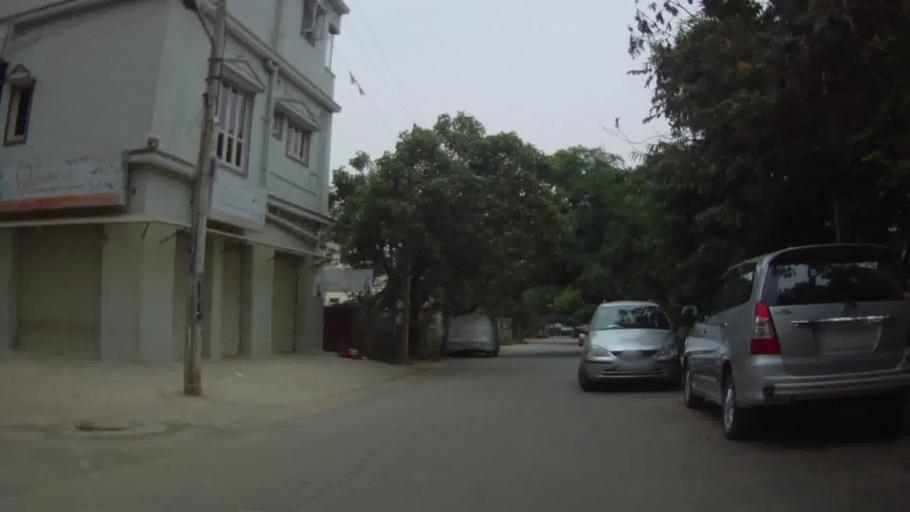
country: IN
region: Karnataka
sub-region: Bangalore Urban
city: Bangalore
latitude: 12.9595
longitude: 77.7193
